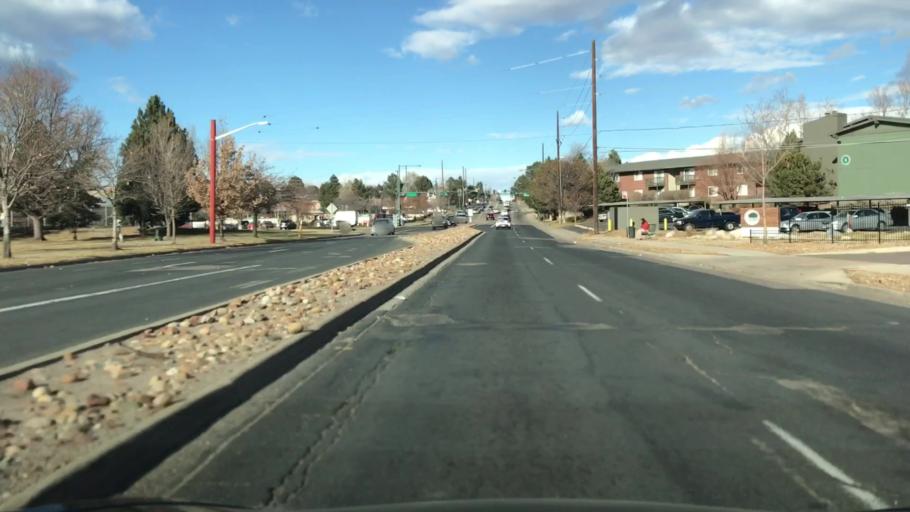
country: US
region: Colorado
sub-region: Arapahoe County
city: Glendale
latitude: 39.6960
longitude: -104.9035
